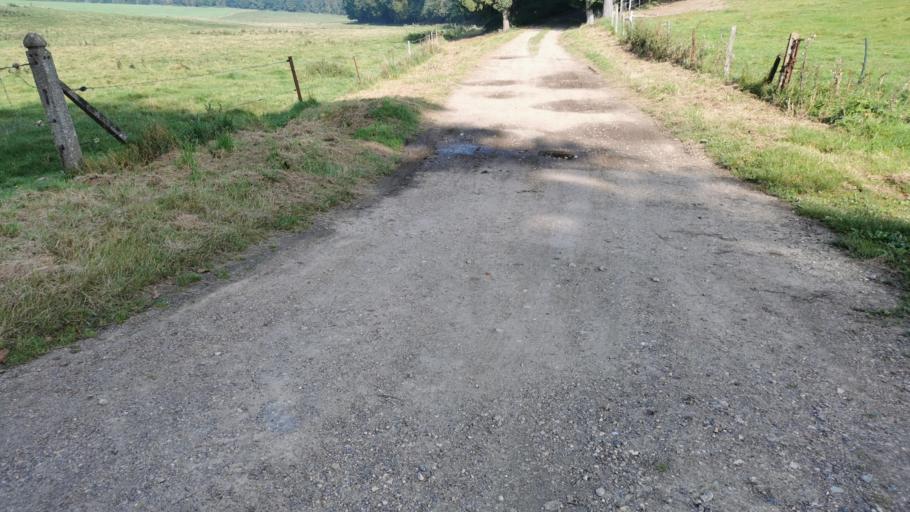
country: FR
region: Haute-Normandie
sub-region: Departement de la Seine-Maritime
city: Valliquerville
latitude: 49.6312
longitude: 0.6887
